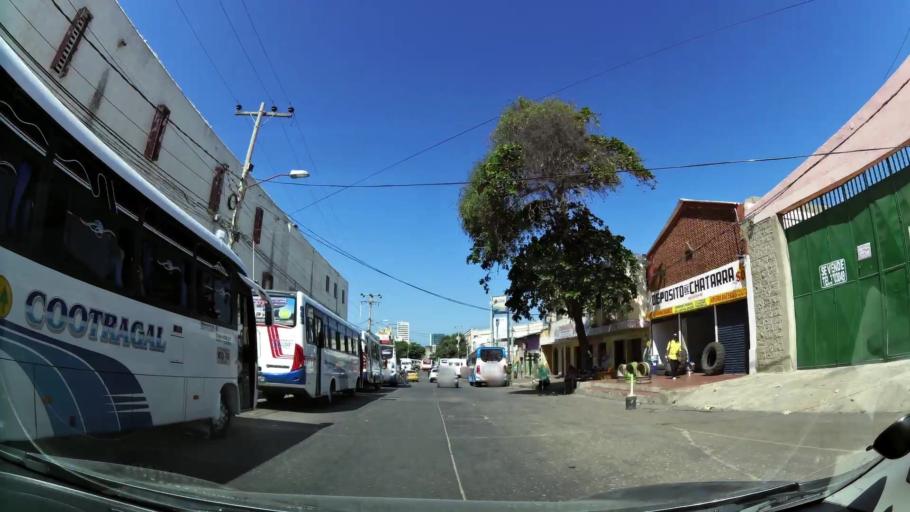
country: CO
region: Atlantico
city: Barranquilla
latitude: 10.9762
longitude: -74.7822
